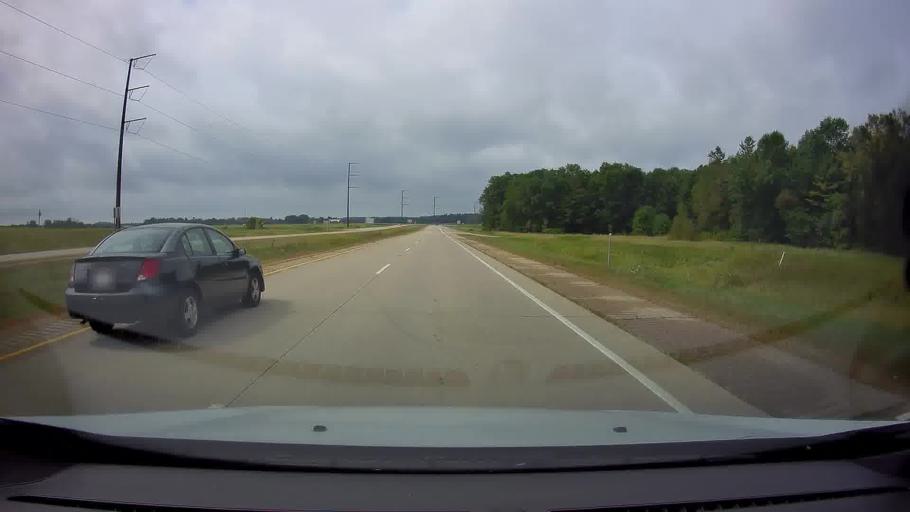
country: US
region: Wisconsin
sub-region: Shawano County
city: Shawano
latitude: 44.7571
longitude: -88.5701
